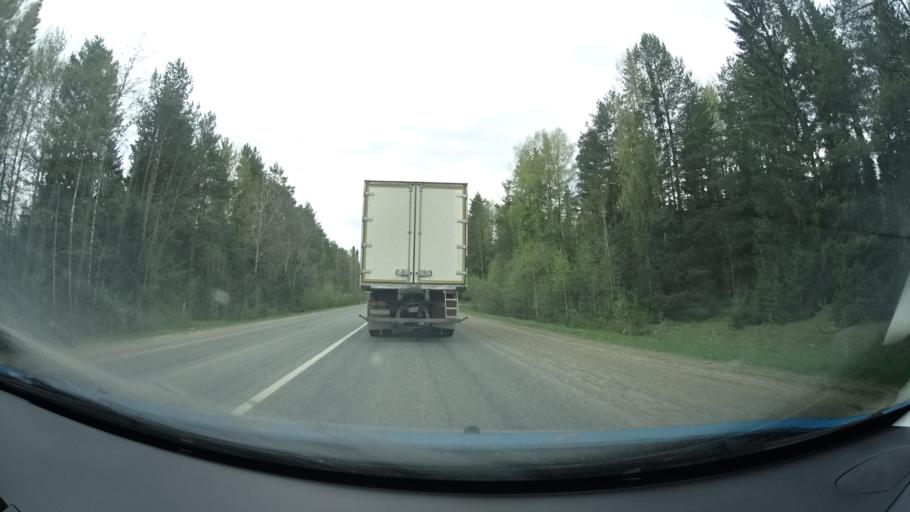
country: RU
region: Perm
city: Yugo-Kamskiy
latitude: 57.5659
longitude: 55.6799
